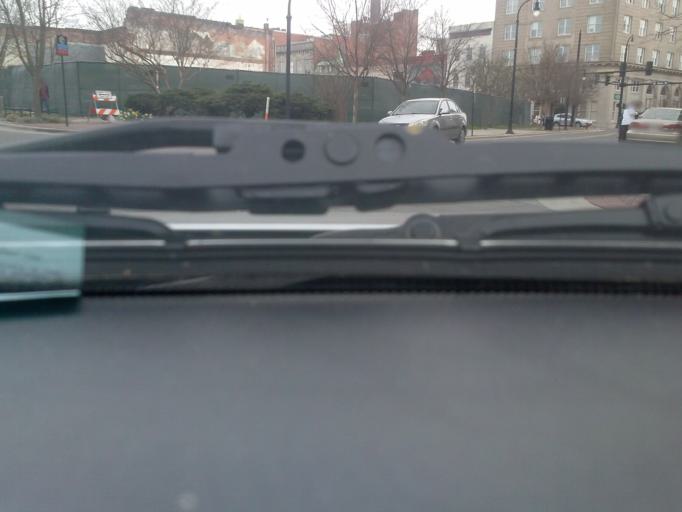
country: US
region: North Carolina
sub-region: Durham County
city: Durham
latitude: 35.9964
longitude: -78.9016
